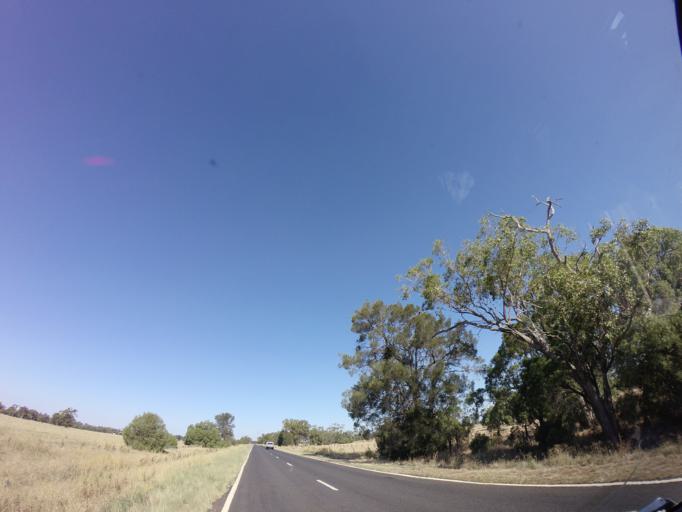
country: AU
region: New South Wales
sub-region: Gilgandra
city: Gilgandra
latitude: -31.6731
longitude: 148.2412
